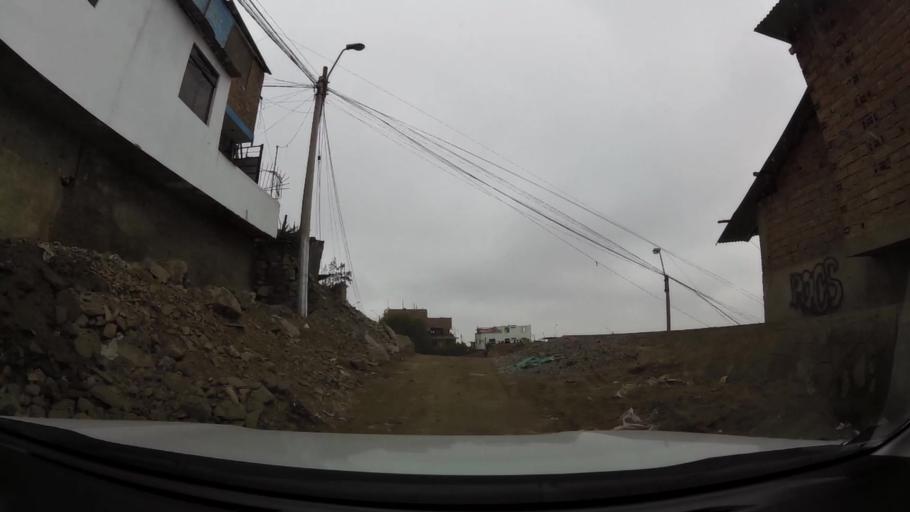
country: PE
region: Lima
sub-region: Lima
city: Surco
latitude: -12.1781
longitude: -76.9555
